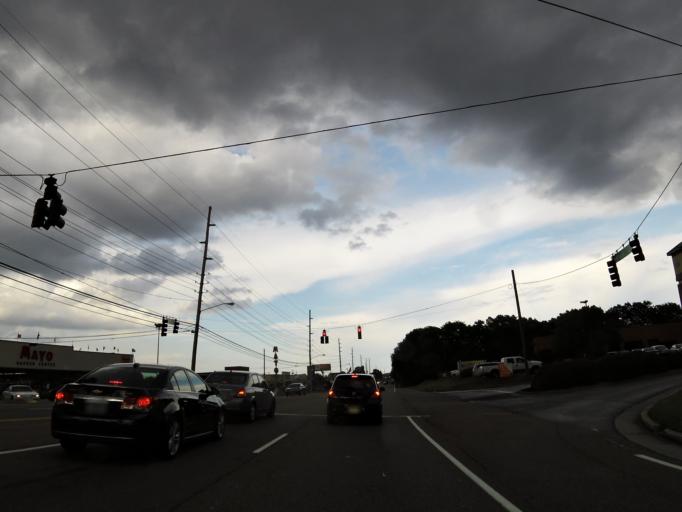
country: US
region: Tennessee
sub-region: Knox County
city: Farragut
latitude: 35.9076
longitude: -84.1063
